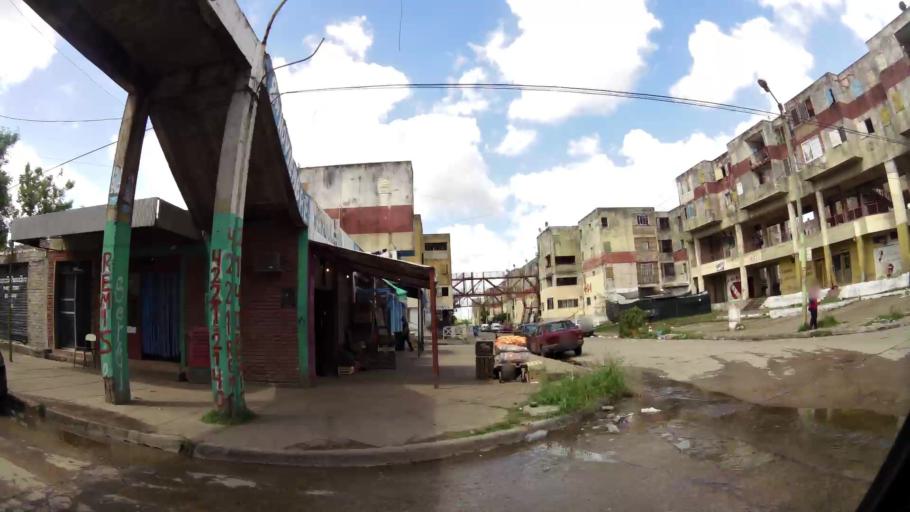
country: AR
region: Buenos Aires
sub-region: Partido de Quilmes
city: Quilmes
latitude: -34.8326
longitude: -58.2219
